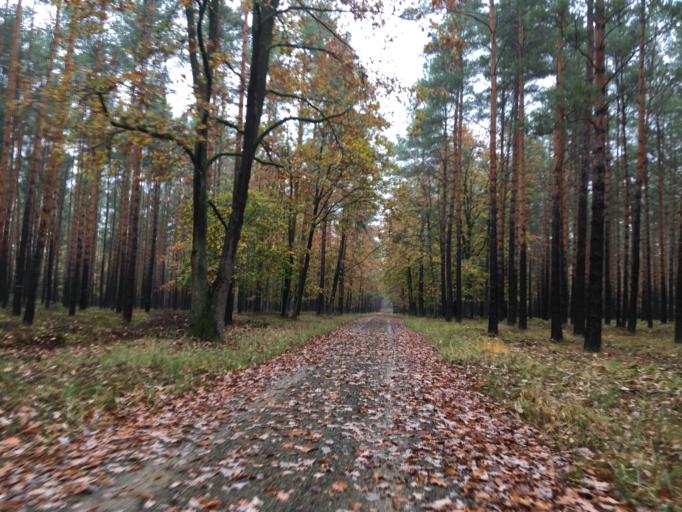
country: DE
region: Brandenburg
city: Beeskow
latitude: 52.2307
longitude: 14.2870
